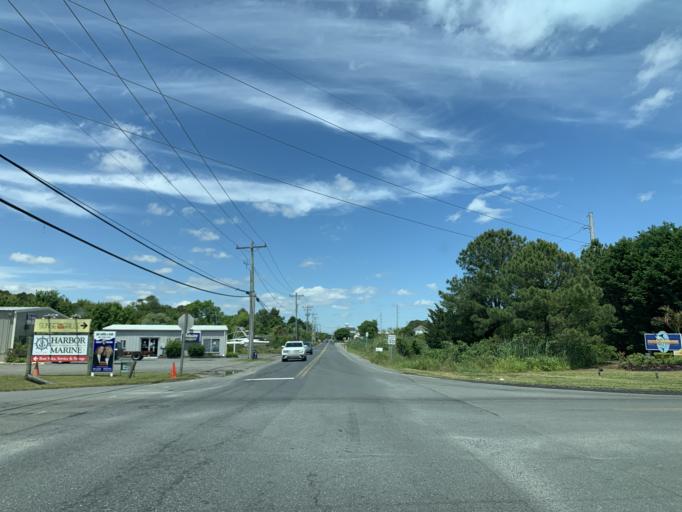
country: US
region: Maryland
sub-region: Worcester County
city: West Ocean City
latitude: 38.3278
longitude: -75.1077
